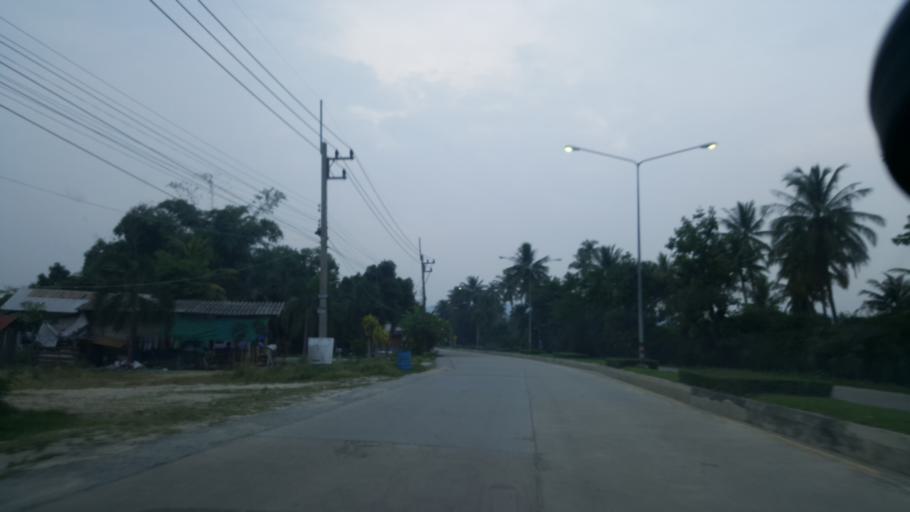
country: TH
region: Chon Buri
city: Si Racha
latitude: 13.2363
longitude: 101.0097
